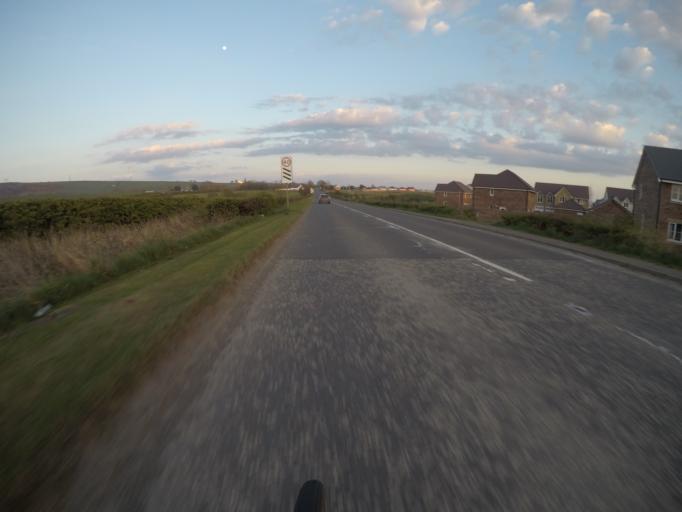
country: GB
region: Scotland
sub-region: South Ayrshire
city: Troon
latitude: 55.5621
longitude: -4.6335
